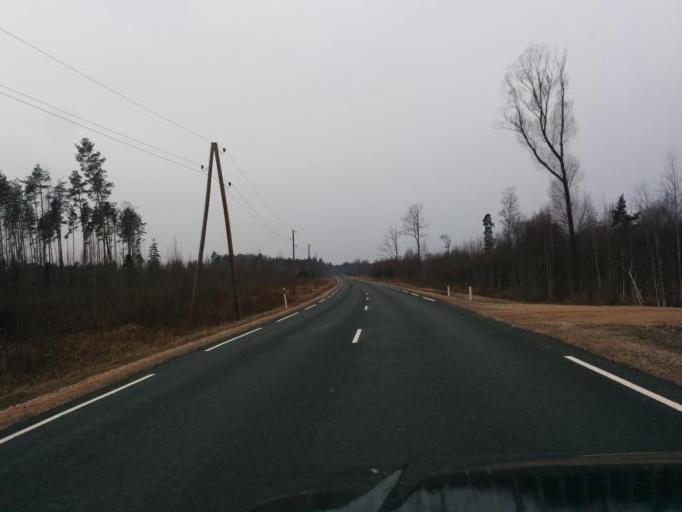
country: LV
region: Ogre
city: Ogre
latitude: 56.8054
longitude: 24.5585
